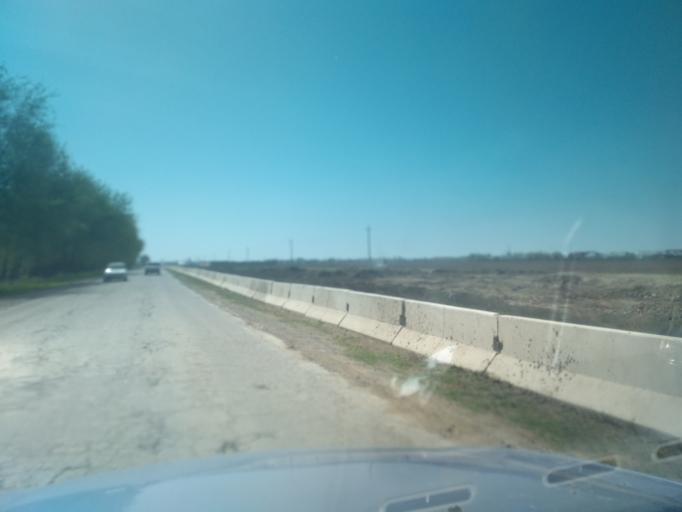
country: UZ
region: Sirdaryo
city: Guliston
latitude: 40.5108
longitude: 68.7953
